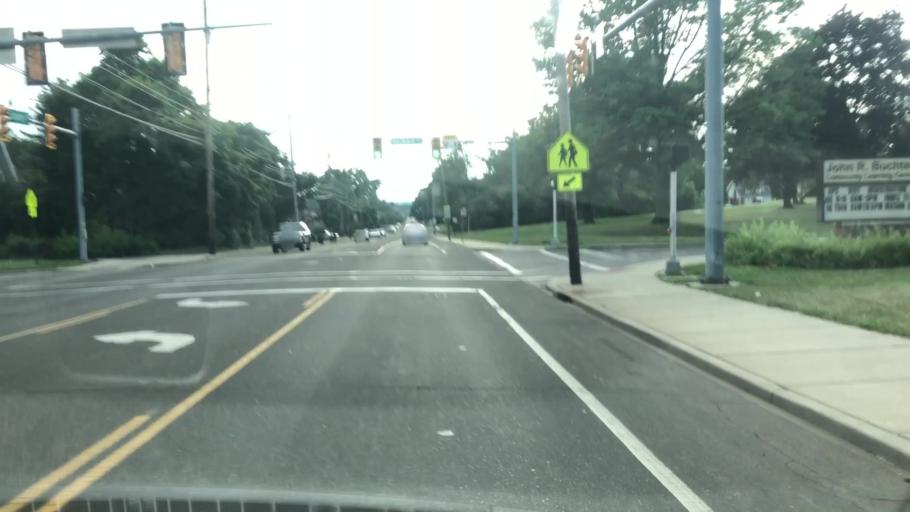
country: US
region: Ohio
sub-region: Summit County
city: Akron
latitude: 41.0840
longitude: -81.5602
